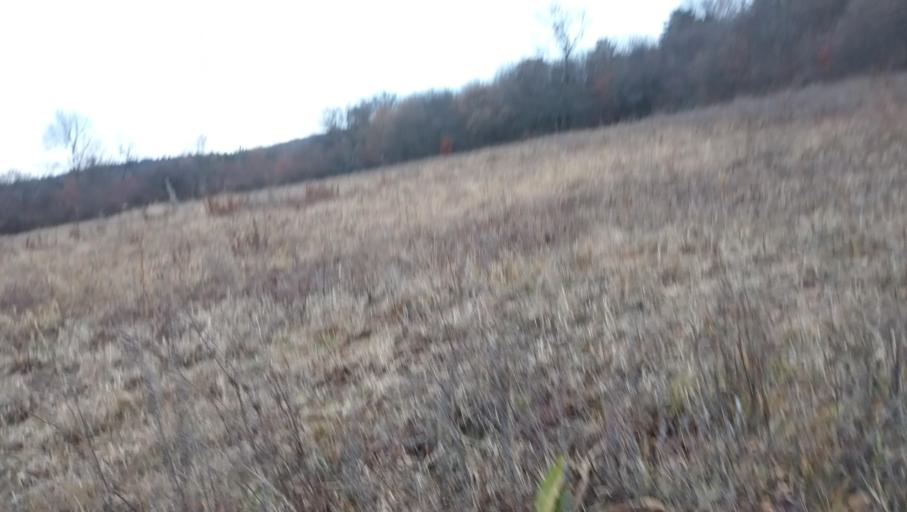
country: HU
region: Pest
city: Urom
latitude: 47.6184
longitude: 19.0158
